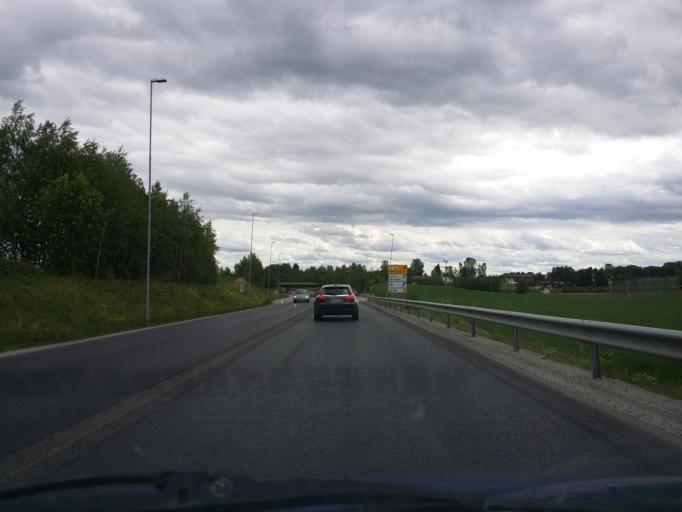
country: NO
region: Hedmark
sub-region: Hamar
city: Hamar
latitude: 60.8364
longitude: 11.0726
